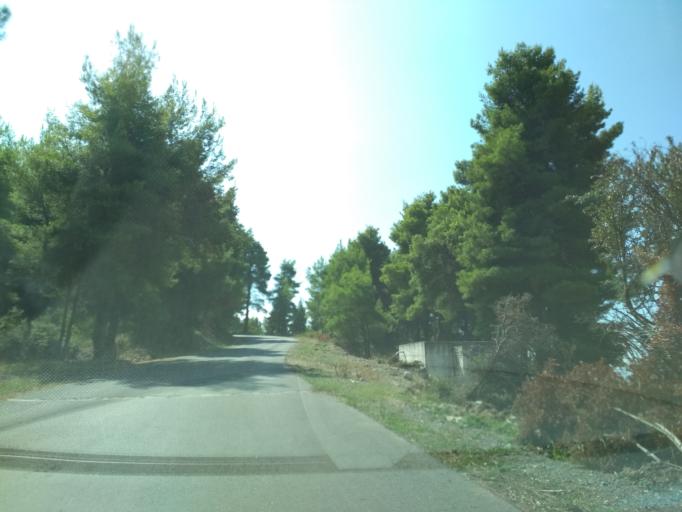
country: GR
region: Central Greece
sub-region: Nomos Evvoias
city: Roviai
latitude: 38.8167
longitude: 23.2736
